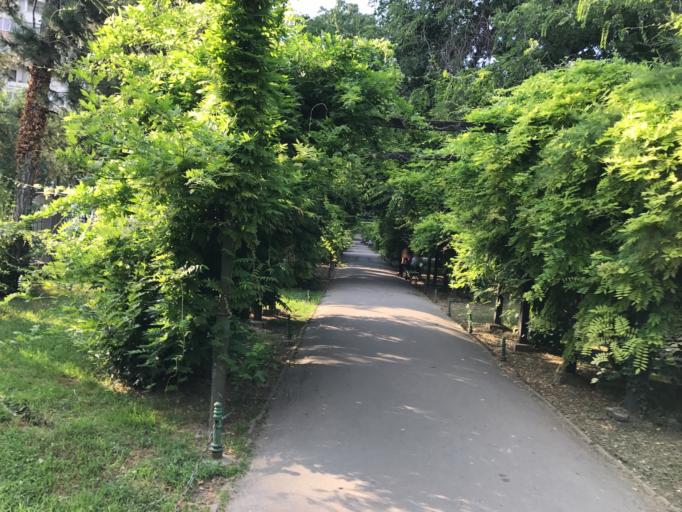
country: RO
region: Bucuresti
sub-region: Municipiul Bucuresti
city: Bucuresti
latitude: 44.4371
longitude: 26.0886
